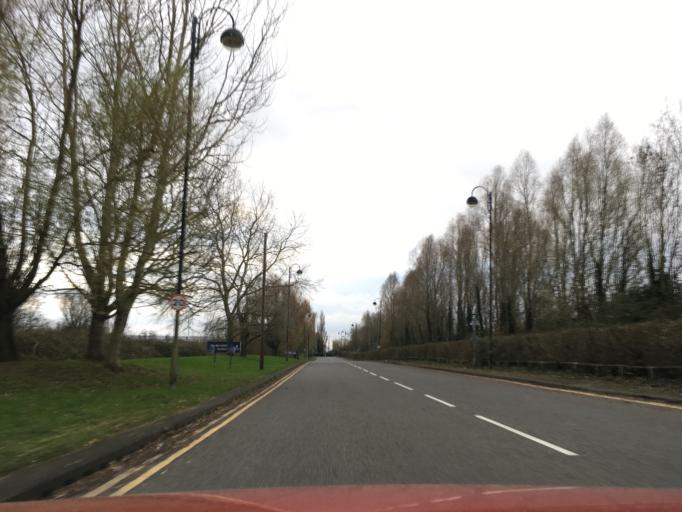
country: GB
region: Wales
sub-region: Newport
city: Bishton
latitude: 51.5767
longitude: -2.8641
